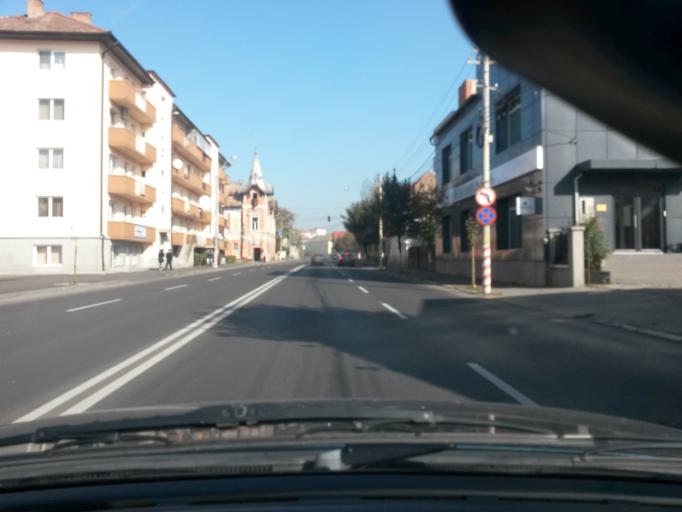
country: RO
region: Mures
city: Targu-Mures
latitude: 46.5356
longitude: 24.5551
